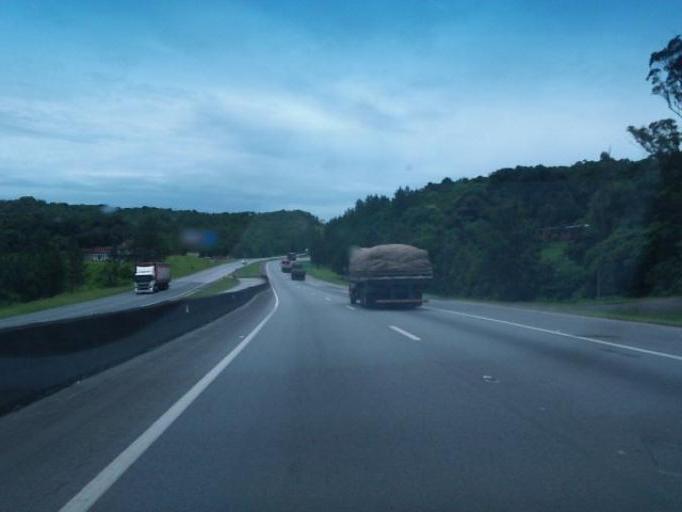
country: BR
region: Sao Paulo
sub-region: Juquitiba
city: Juquitiba
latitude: -23.9525
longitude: -47.1045
